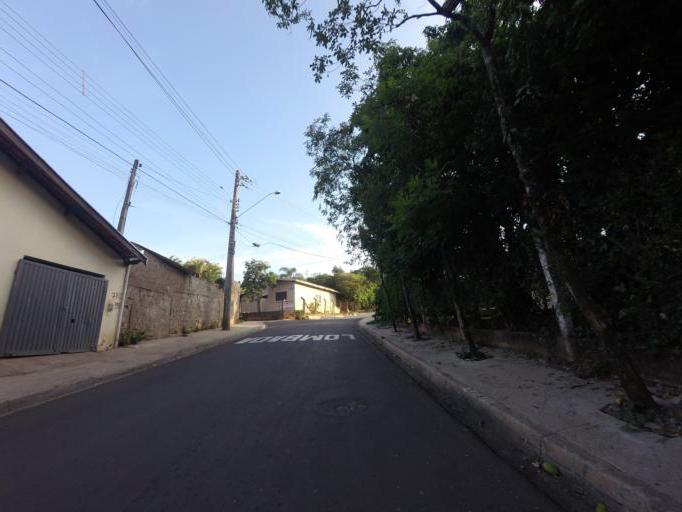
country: BR
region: Sao Paulo
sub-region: Piracicaba
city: Piracicaba
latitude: -22.7488
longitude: -47.6098
